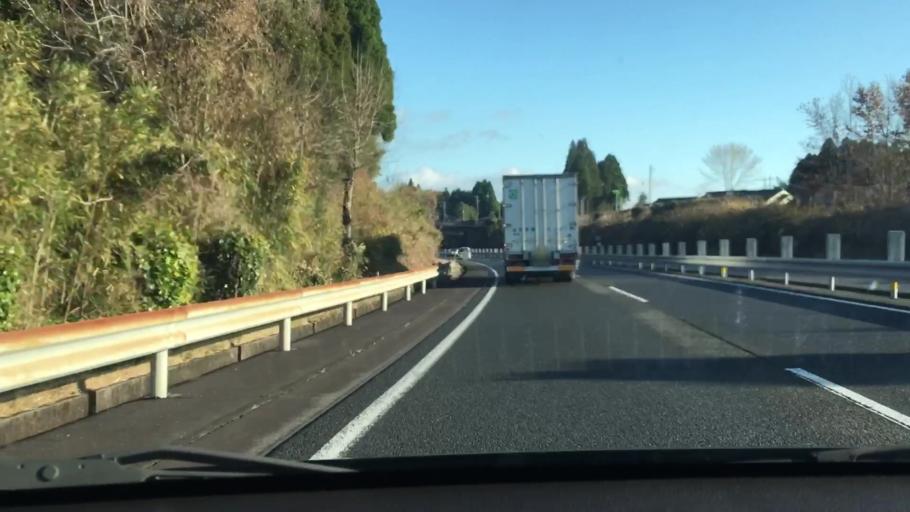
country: JP
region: Kagoshima
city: Kajiki
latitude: 31.8210
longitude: 130.6958
